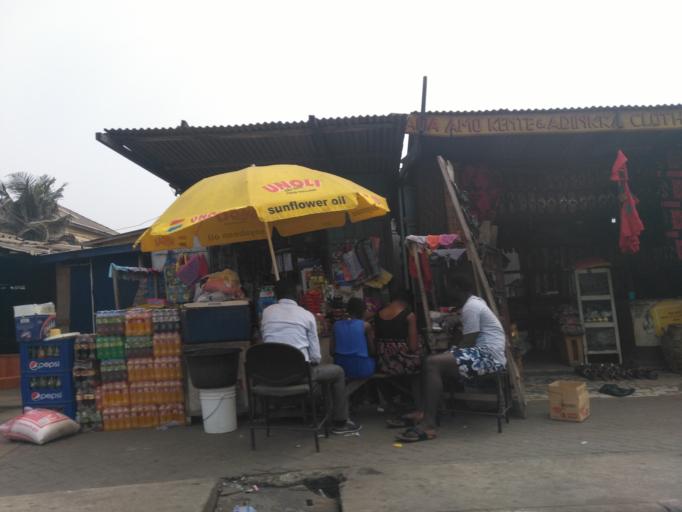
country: GH
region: Greater Accra
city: Accra
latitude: 5.5382
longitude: -0.2169
